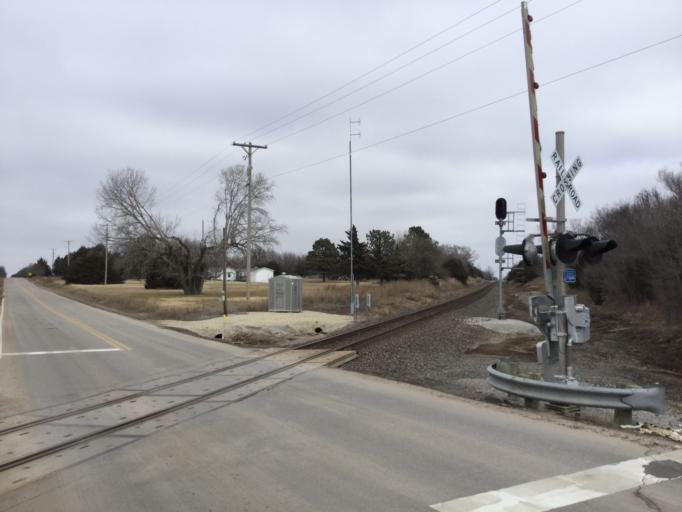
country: US
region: Kansas
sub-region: Sumner County
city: Mulvane
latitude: 37.5008
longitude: -97.2263
